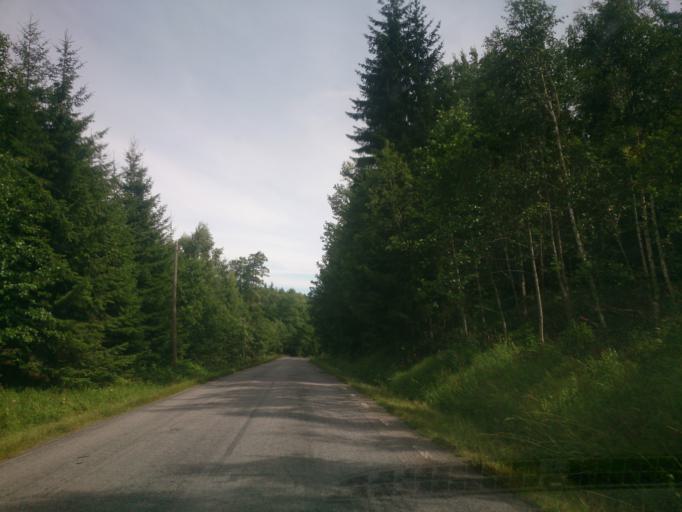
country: SE
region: OEstergoetland
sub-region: Soderkopings Kommun
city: Soederkoeping
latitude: 58.2984
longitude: 16.2533
